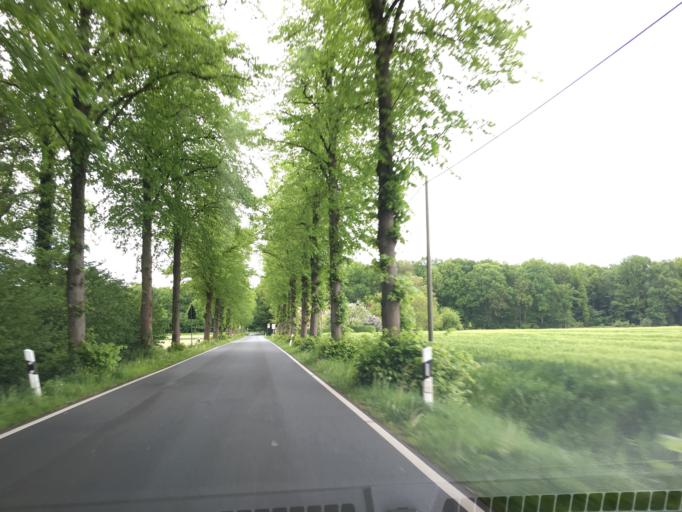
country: DE
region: North Rhine-Westphalia
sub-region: Regierungsbezirk Munster
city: Senden
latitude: 51.9300
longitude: 7.5145
